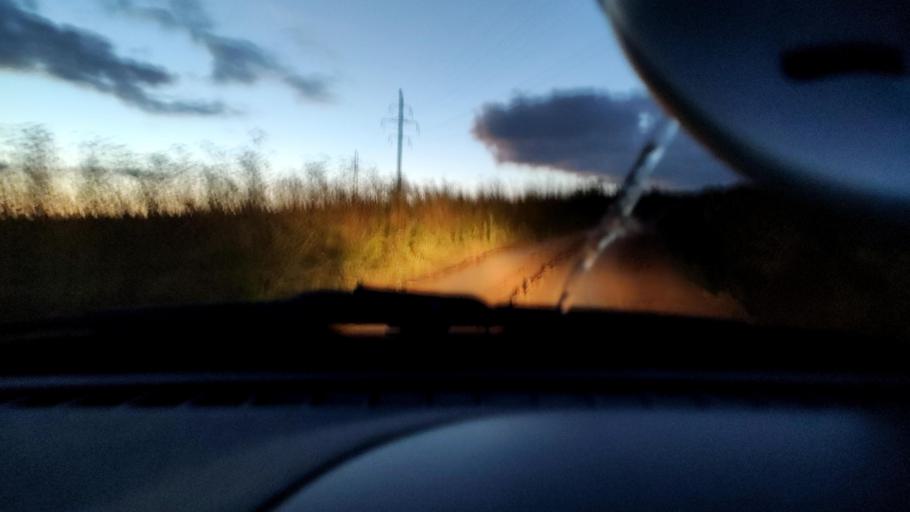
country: RU
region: Perm
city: Froly
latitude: 57.9424
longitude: 56.2529
